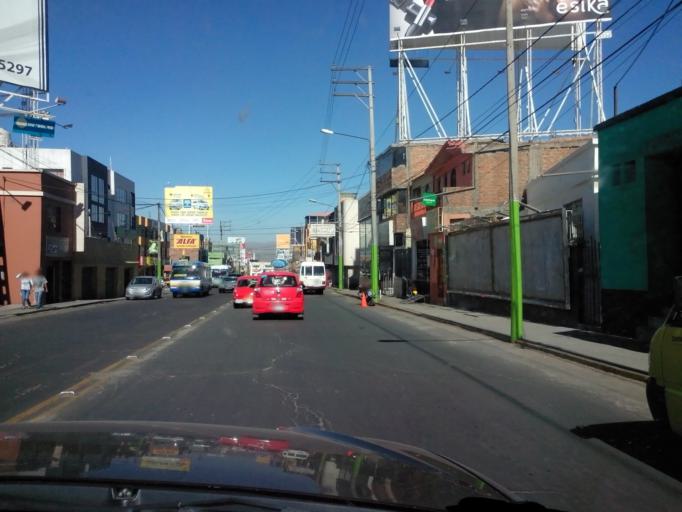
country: PE
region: Arequipa
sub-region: Provincia de Arequipa
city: Arequipa
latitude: -16.3849
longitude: -71.5552
